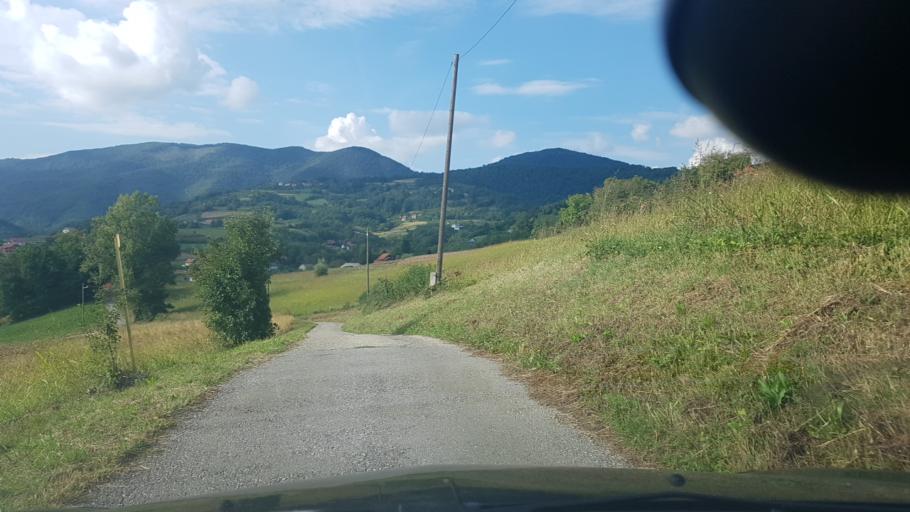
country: HR
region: Krapinsko-Zagorska
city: Radoboj
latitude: 46.1583
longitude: 15.9344
